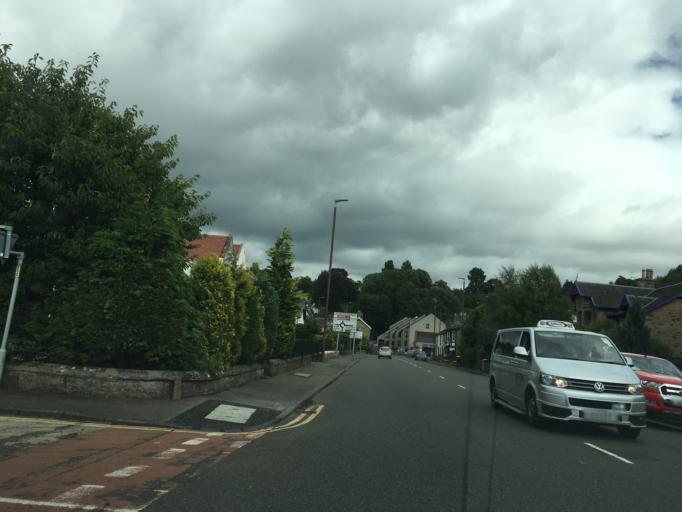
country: GB
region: Scotland
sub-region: Stirling
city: Stirling
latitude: 56.1374
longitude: -3.9249
